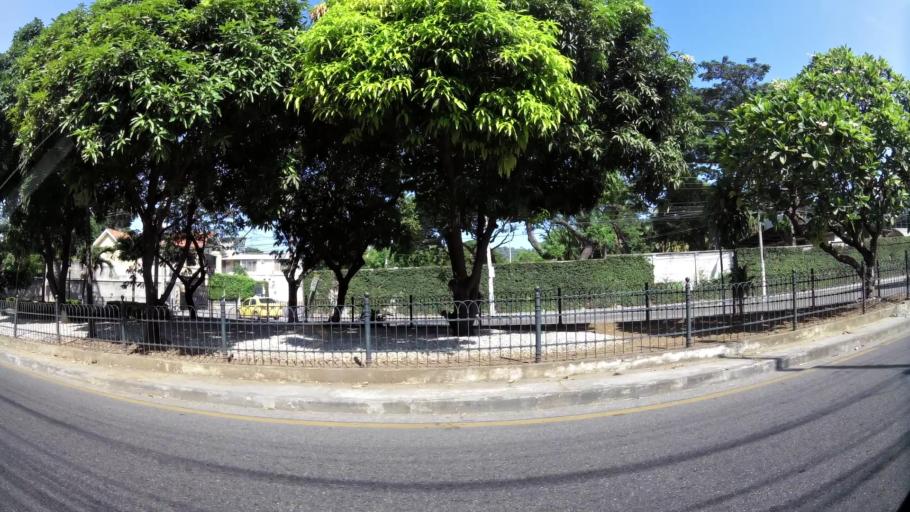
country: EC
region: Guayas
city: Guayaquil
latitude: -2.1657
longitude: -79.9431
